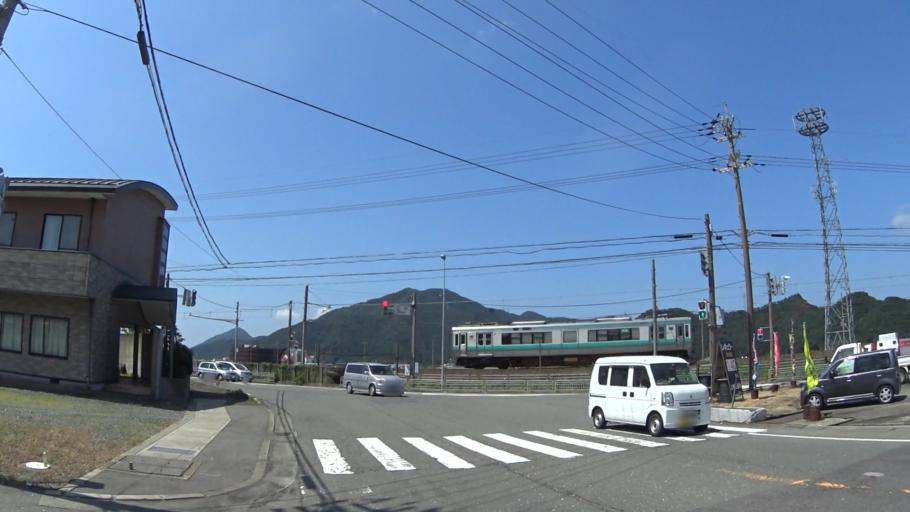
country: JP
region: Fukui
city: Obama
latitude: 35.4625
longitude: 135.8625
